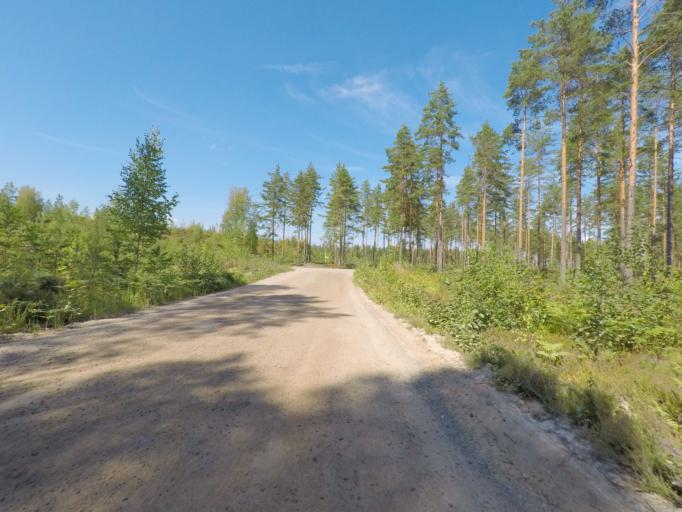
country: FI
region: Southern Savonia
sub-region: Mikkeli
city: Puumala
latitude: 61.4174
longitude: 28.0423
